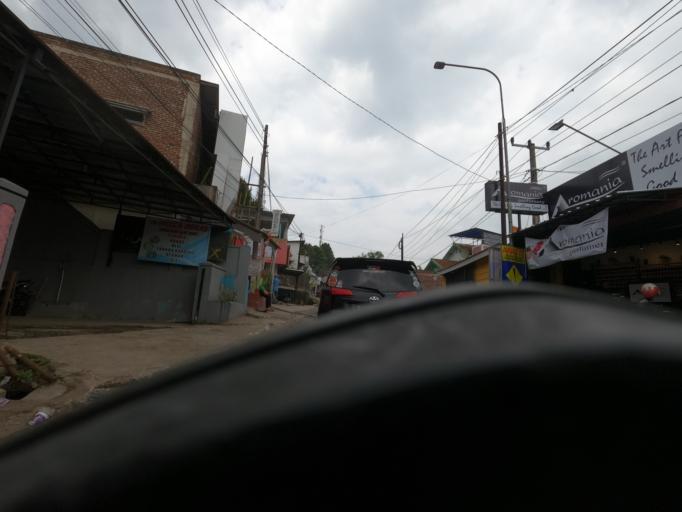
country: ID
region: West Java
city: Lembang
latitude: -6.8127
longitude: 107.5595
